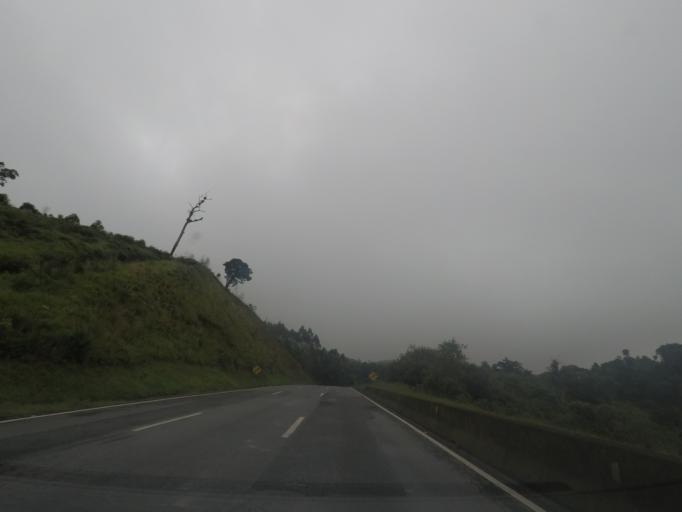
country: BR
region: Parana
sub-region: Antonina
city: Antonina
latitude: -25.0397
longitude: -48.5487
